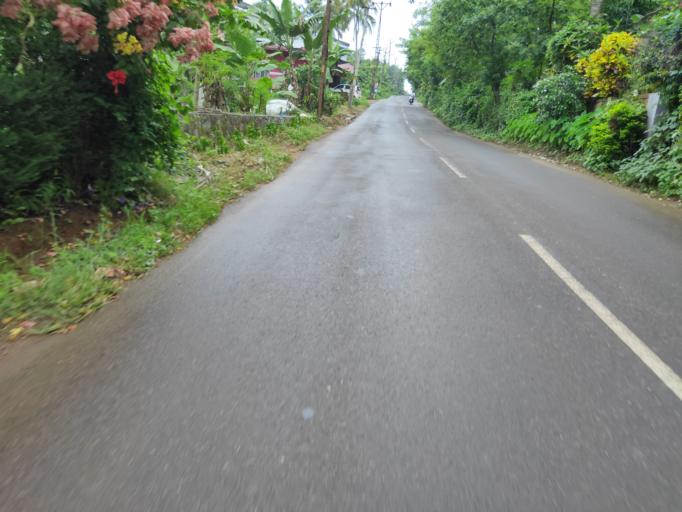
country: IN
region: Kerala
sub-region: Malappuram
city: Manjeri
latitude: 11.2264
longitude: 76.2719
